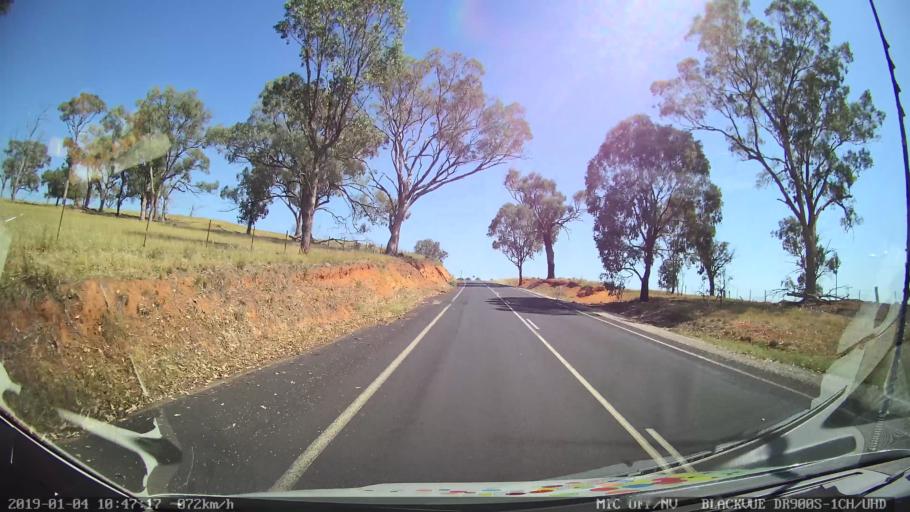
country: AU
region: New South Wales
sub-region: Cabonne
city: Molong
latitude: -33.2715
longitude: 148.7200
